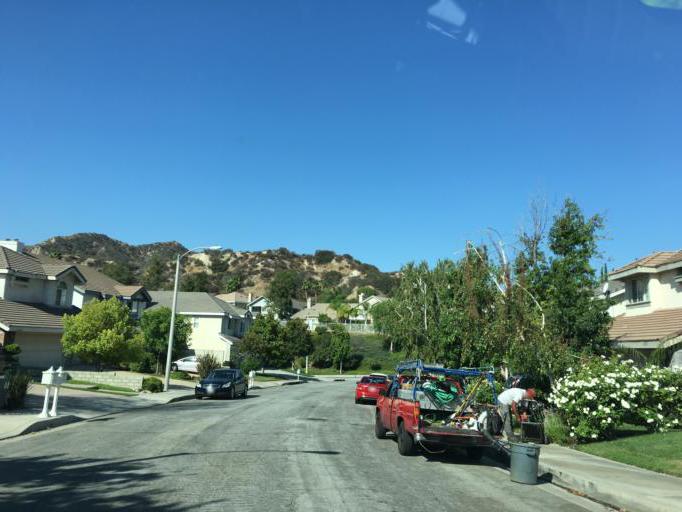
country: US
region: California
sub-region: Los Angeles County
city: Santa Clarita
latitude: 34.3865
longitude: -118.5851
